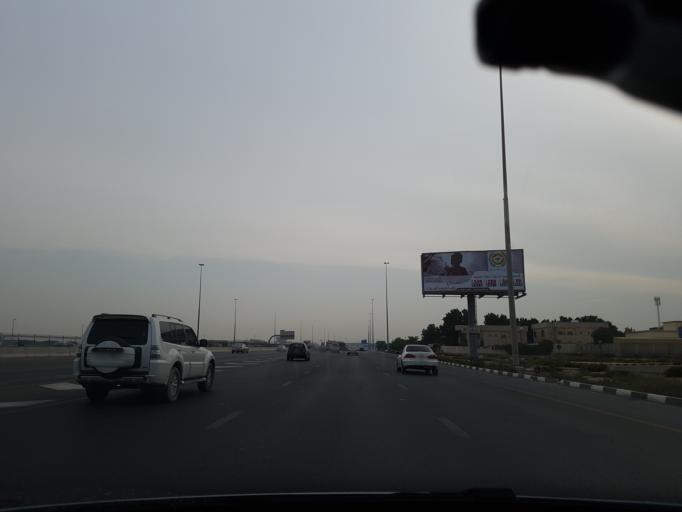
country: AE
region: Ash Shariqah
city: Sharjah
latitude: 25.3553
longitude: 55.4797
